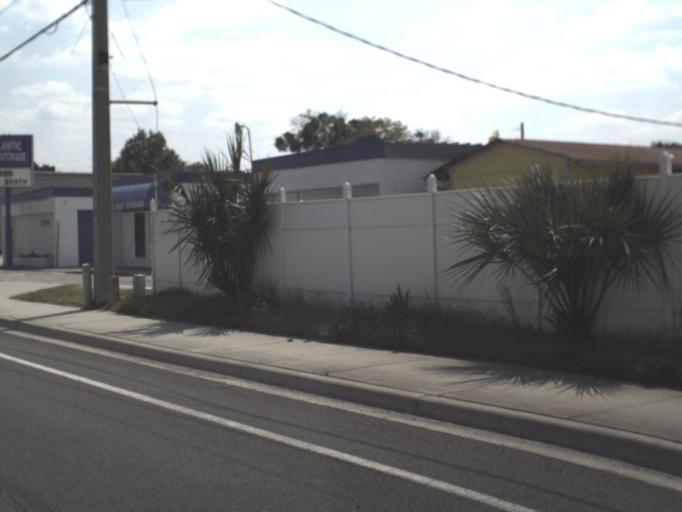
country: US
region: Florida
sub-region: Duval County
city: Atlantic Beach
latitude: 30.3271
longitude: -81.4186
